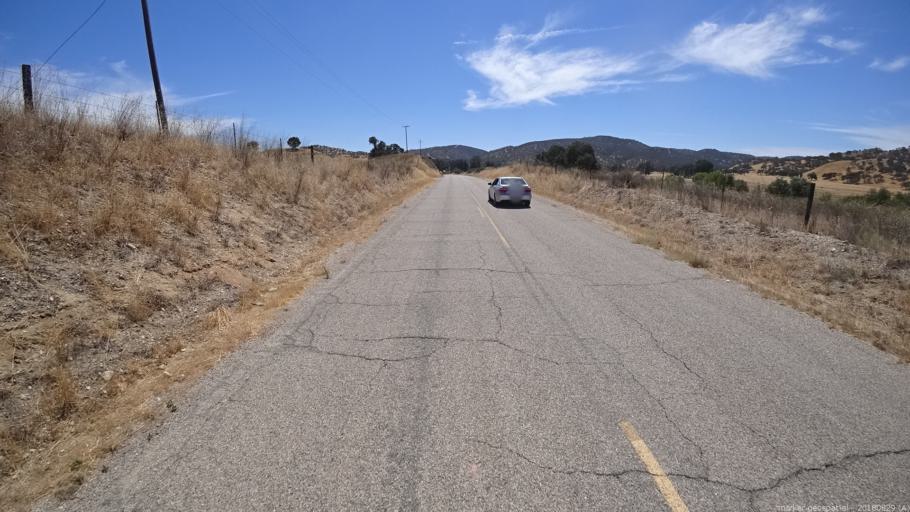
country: US
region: California
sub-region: San Luis Obispo County
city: Lake Nacimiento
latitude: 35.8057
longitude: -120.8556
